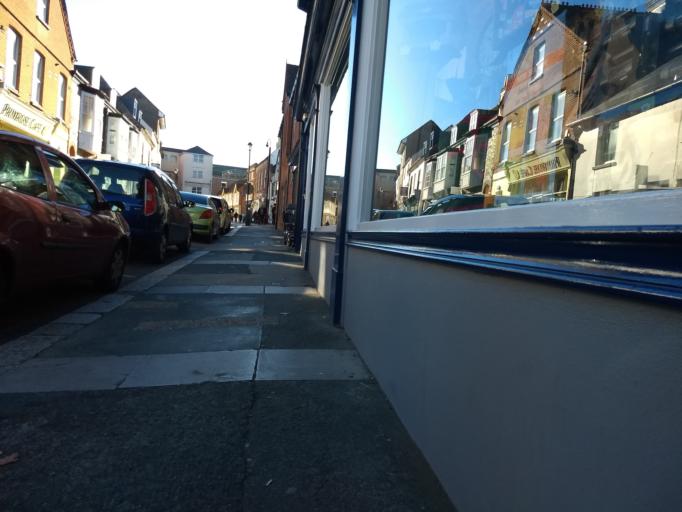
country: GB
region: England
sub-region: Isle of Wight
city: Newport
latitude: 50.7014
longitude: -1.2939
